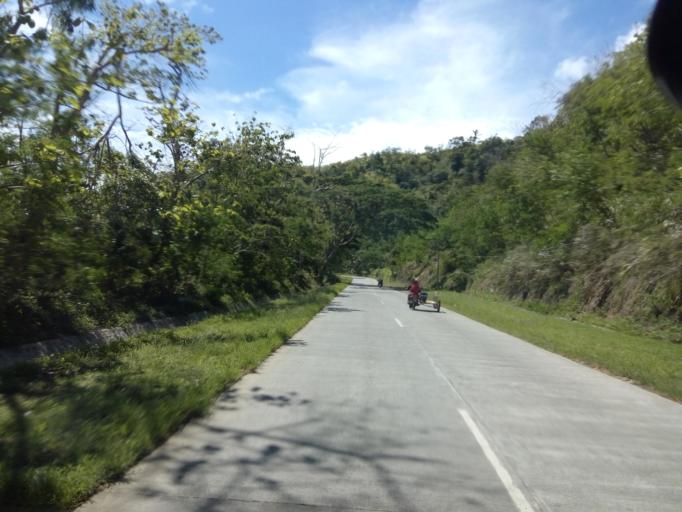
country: PH
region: Central Luzon
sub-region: Province of Nueva Ecija
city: General Luna
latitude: 15.7980
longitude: 121.2831
